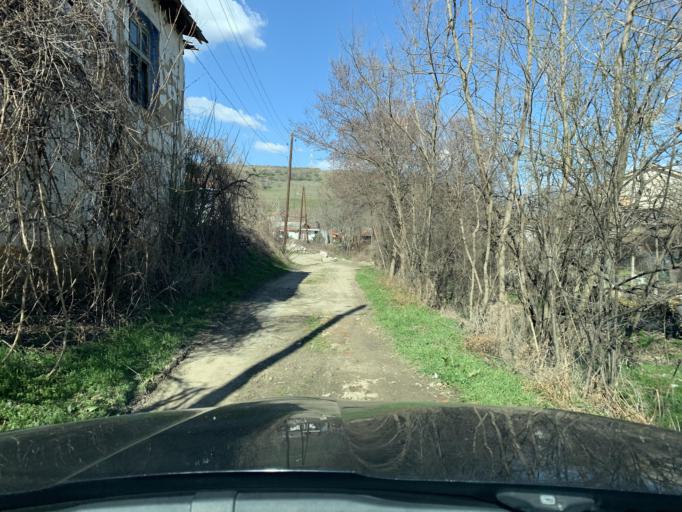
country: MK
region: Demir Kapija
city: Demir Kapija
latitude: 41.4187
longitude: 22.1661
